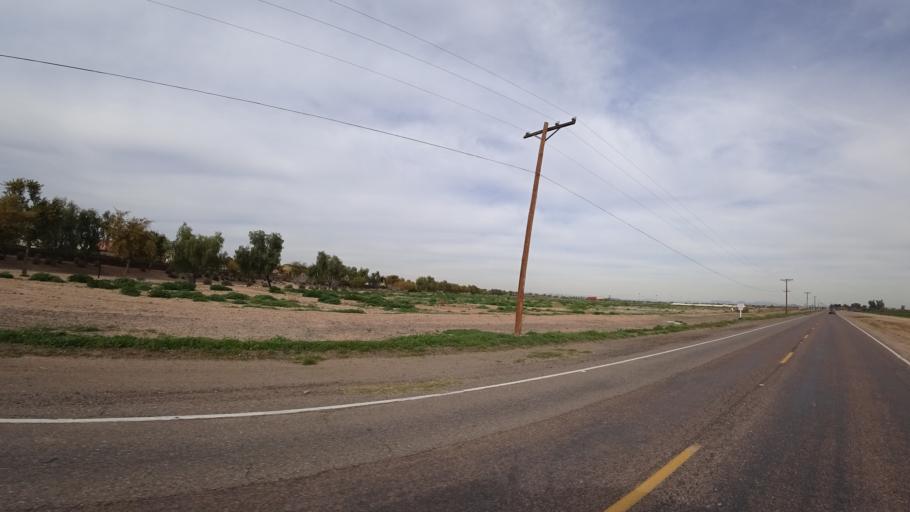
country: US
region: Arizona
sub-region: Maricopa County
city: Citrus Park
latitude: 33.5805
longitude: -112.3906
